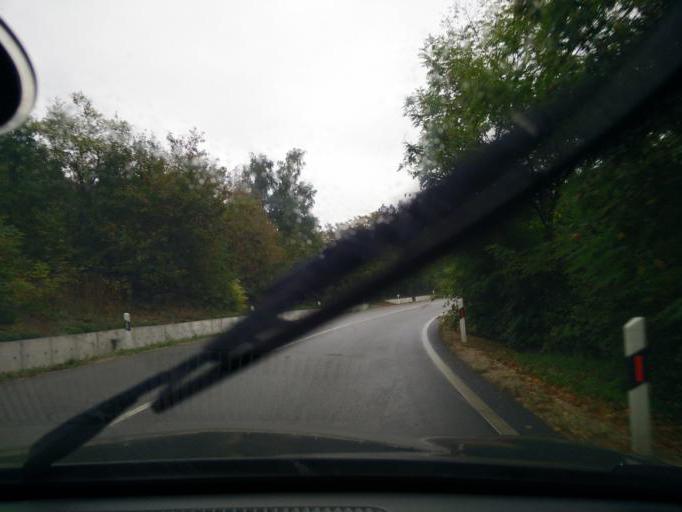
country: HU
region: Komarom-Esztergom
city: Tarjan
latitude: 47.6427
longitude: 18.5398
